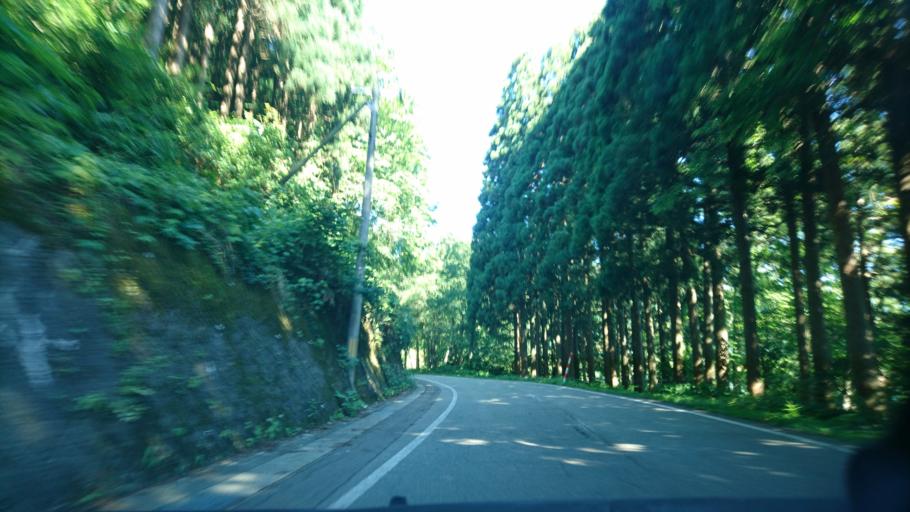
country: JP
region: Akita
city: Kakunodatemachi
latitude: 39.7143
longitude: 140.6335
